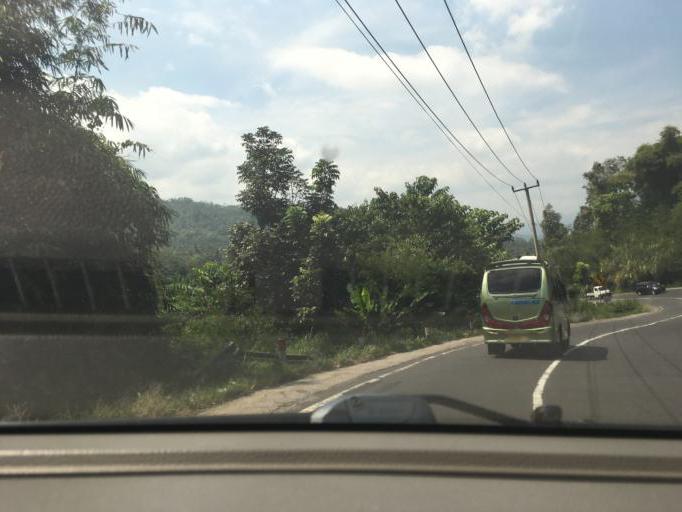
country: ID
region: West Java
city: Wage Cibahayu
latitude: -7.1156
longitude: 108.1229
